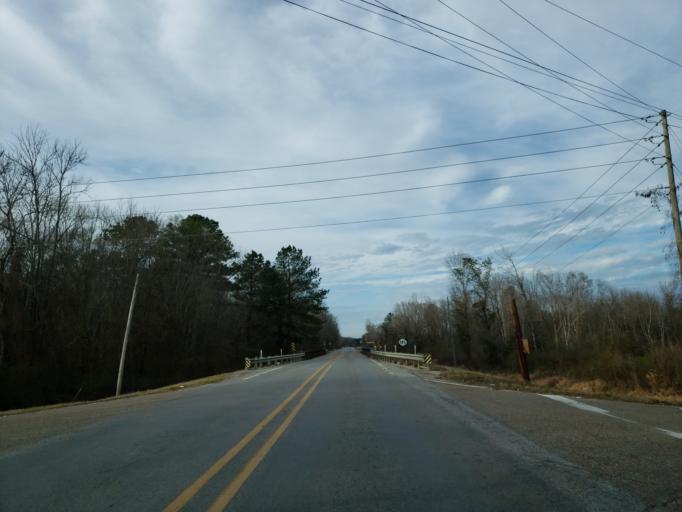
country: US
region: Mississippi
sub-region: Clarke County
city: Quitman
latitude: 31.8615
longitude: -88.7001
